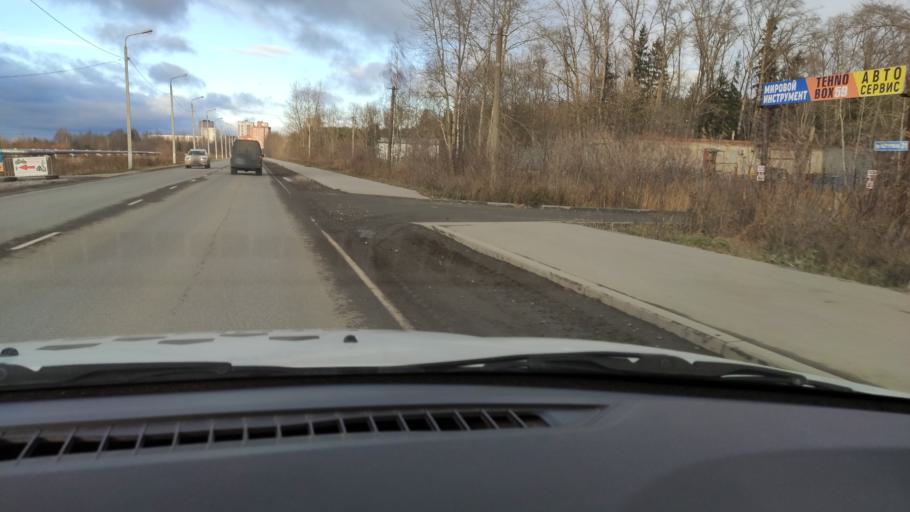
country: RU
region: Perm
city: Kondratovo
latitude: 57.9798
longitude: 56.1310
